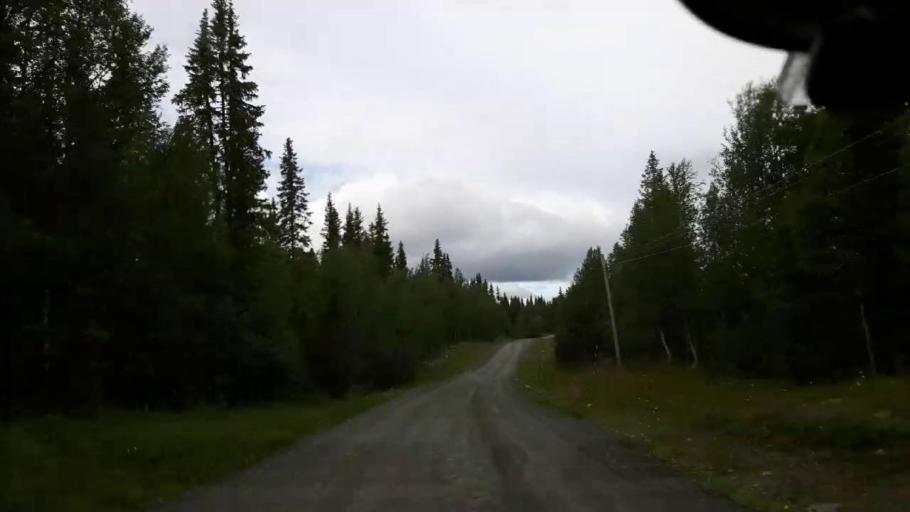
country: SE
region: Jaemtland
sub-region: Krokoms Kommun
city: Valla
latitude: 63.7284
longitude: 13.8390
